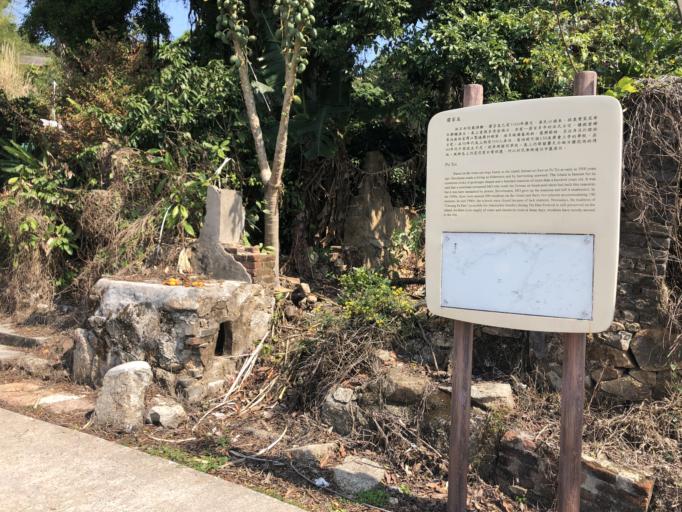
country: HK
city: Sok Kwu Wan
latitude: 22.1633
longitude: 114.2538
